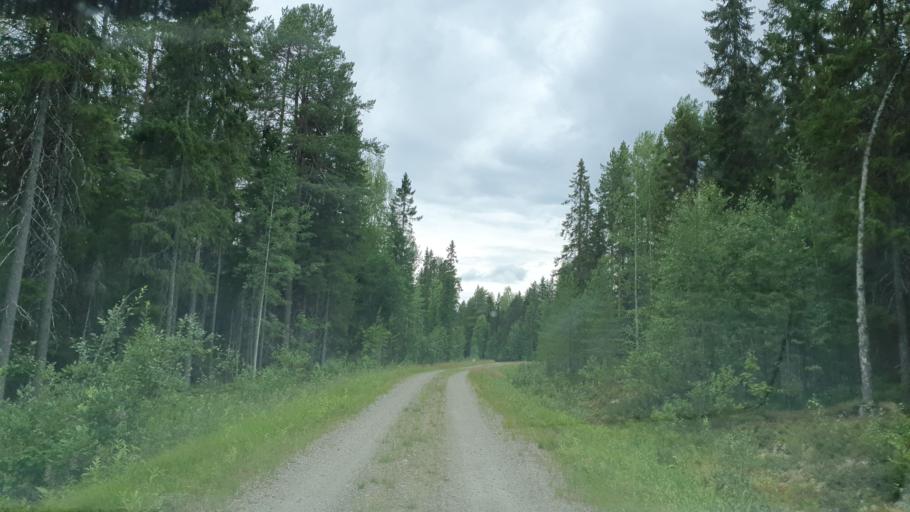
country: FI
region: Kainuu
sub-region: Kehys-Kainuu
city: Kuhmo
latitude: 64.2020
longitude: 29.3874
